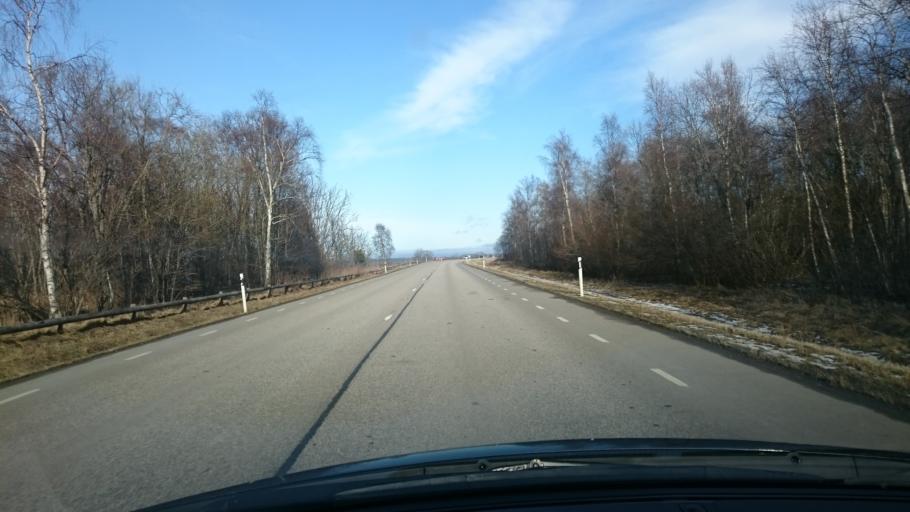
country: EE
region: Harju
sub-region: Keila linn
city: Keila
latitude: 59.4181
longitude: 24.3175
